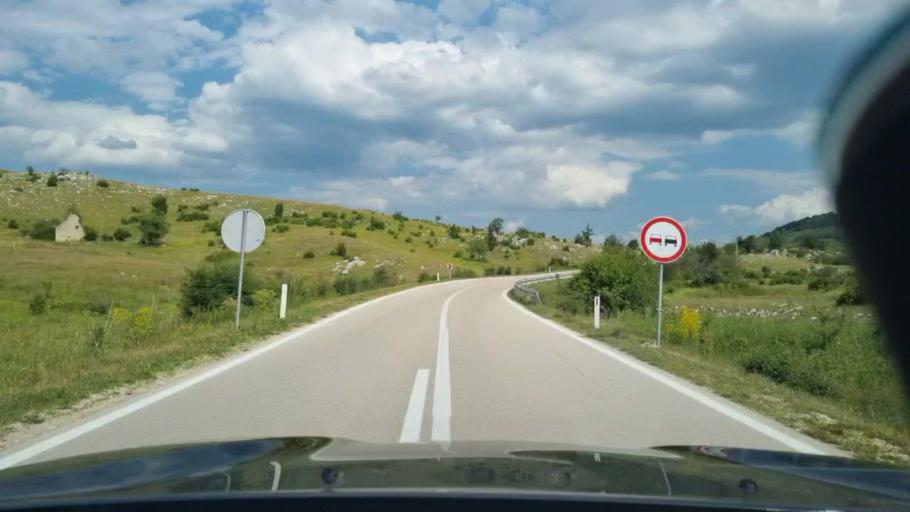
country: BA
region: Federation of Bosnia and Herzegovina
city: Bosansko Grahovo
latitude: 44.1309
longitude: 16.4906
